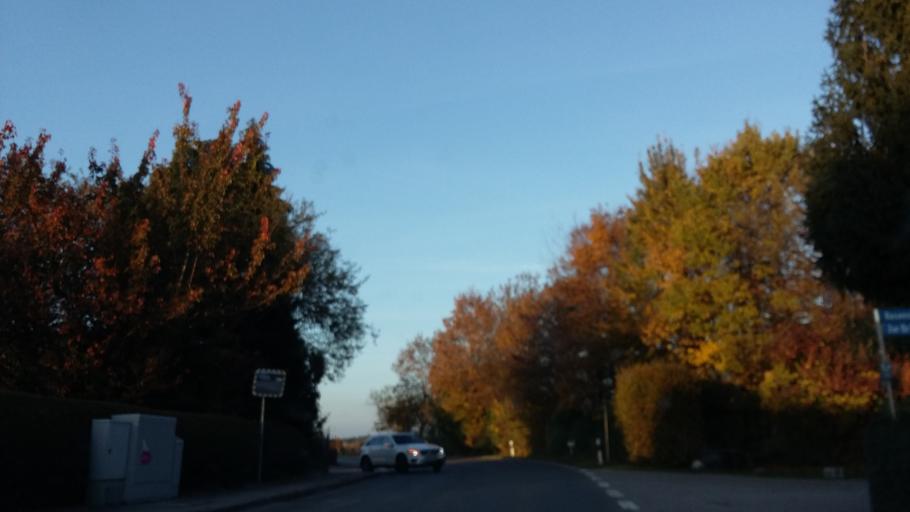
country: DE
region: Bavaria
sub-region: Upper Bavaria
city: Rimsting
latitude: 47.8843
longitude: 12.3403
